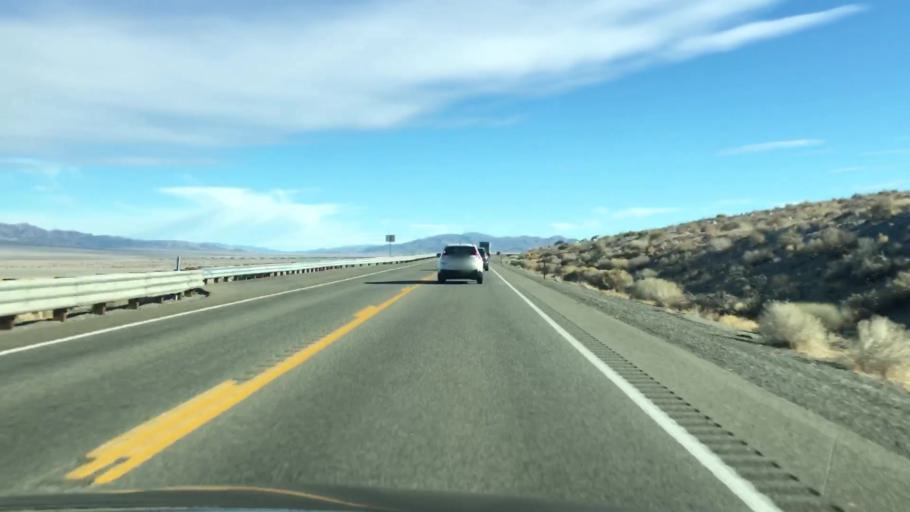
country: US
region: Nevada
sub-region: Mineral County
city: Hawthorne
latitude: 38.6136
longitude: -118.7231
